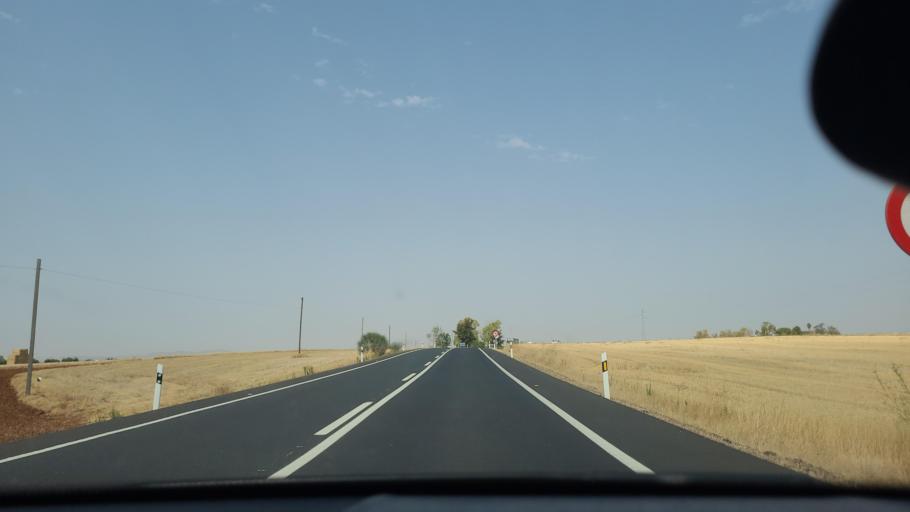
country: ES
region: Extremadura
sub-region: Provincia de Badajoz
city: Berlanga
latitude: 38.2655
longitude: -5.7588
